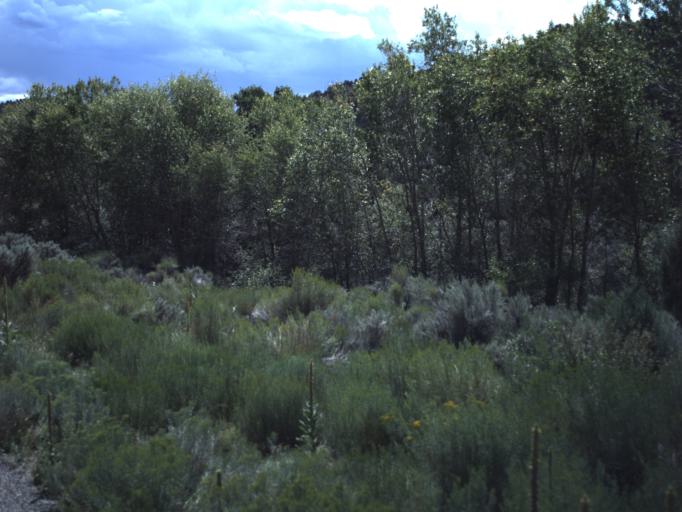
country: US
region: Utah
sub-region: Piute County
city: Junction
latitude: 38.2591
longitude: -112.2745
